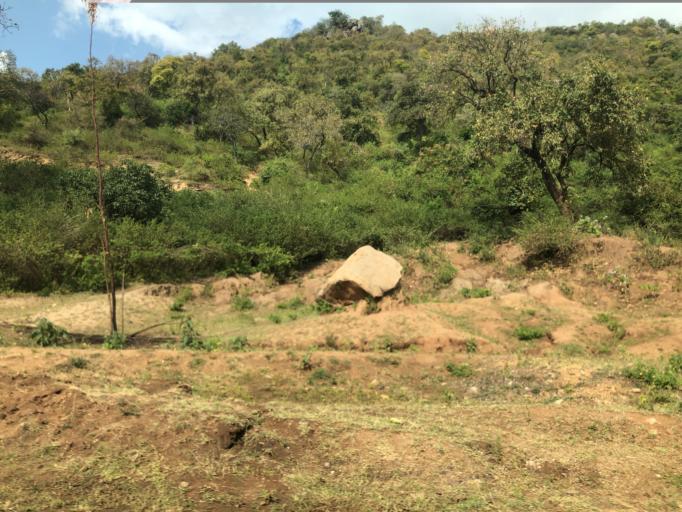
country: ET
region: Southern Nations, Nationalities, and People's Region
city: Bako
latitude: 5.7510
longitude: 36.5894
